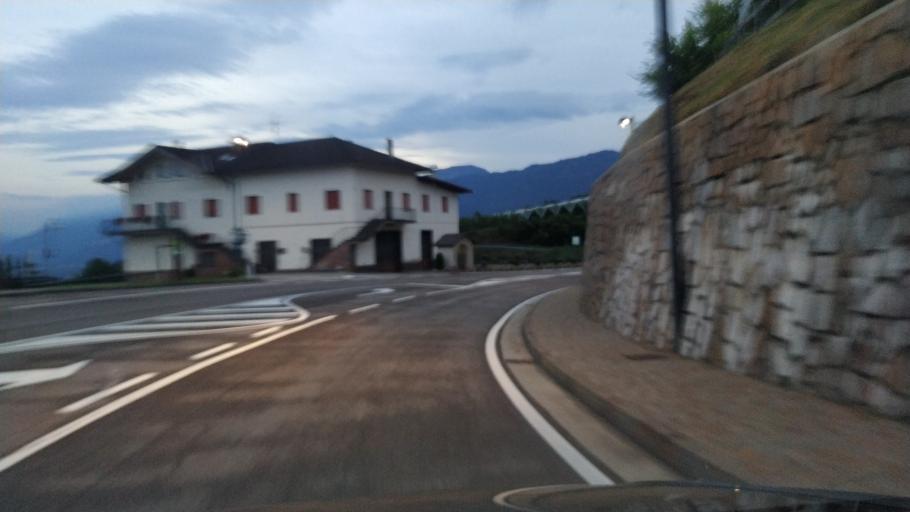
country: IT
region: Trentino-Alto Adige
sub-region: Provincia di Trento
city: Cloz
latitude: 46.4141
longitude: 11.0823
